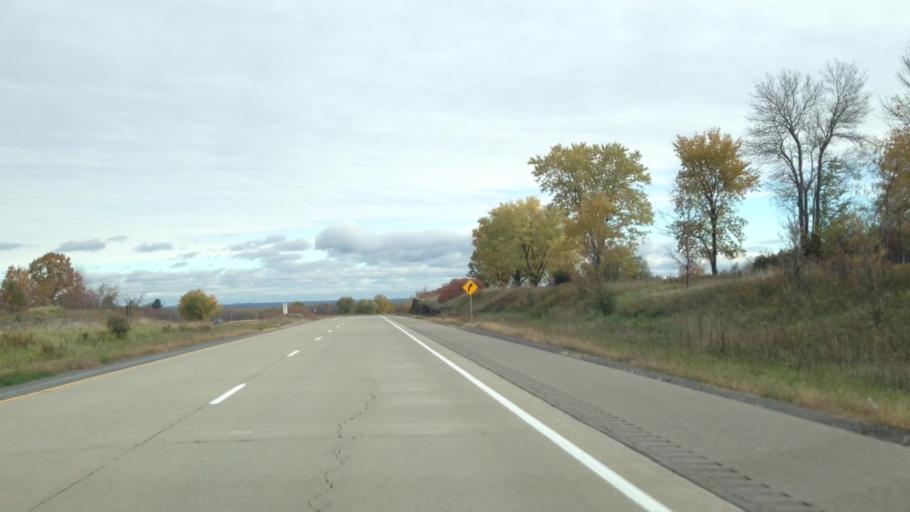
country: CA
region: Ontario
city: Hawkesbury
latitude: 45.5596
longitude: -74.5131
